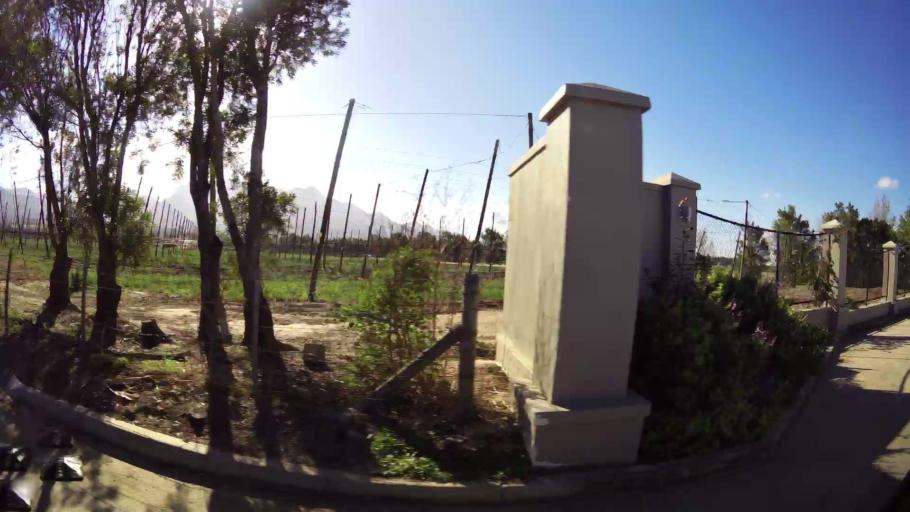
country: ZA
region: Western Cape
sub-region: Eden District Municipality
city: George
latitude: -33.9615
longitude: 22.3995
